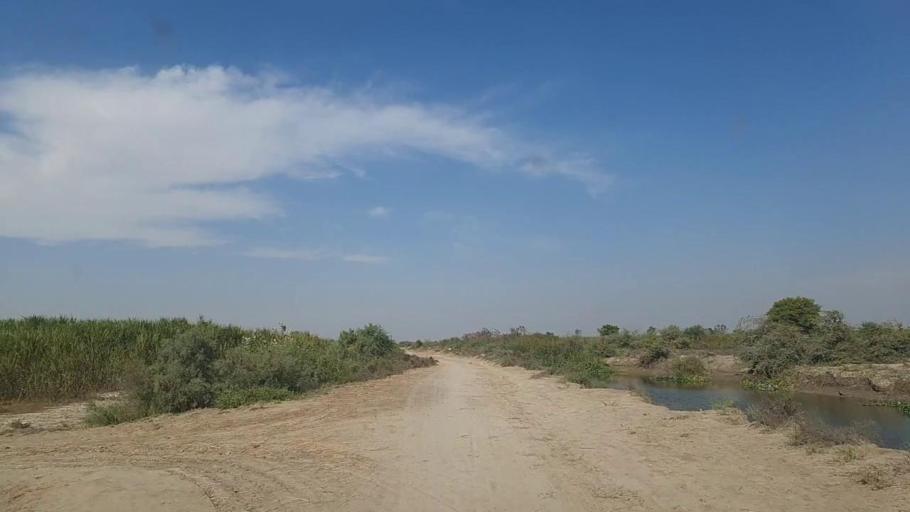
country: PK
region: Sindh
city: Mirpur Batoro
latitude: 24.7978
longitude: 68.2697
